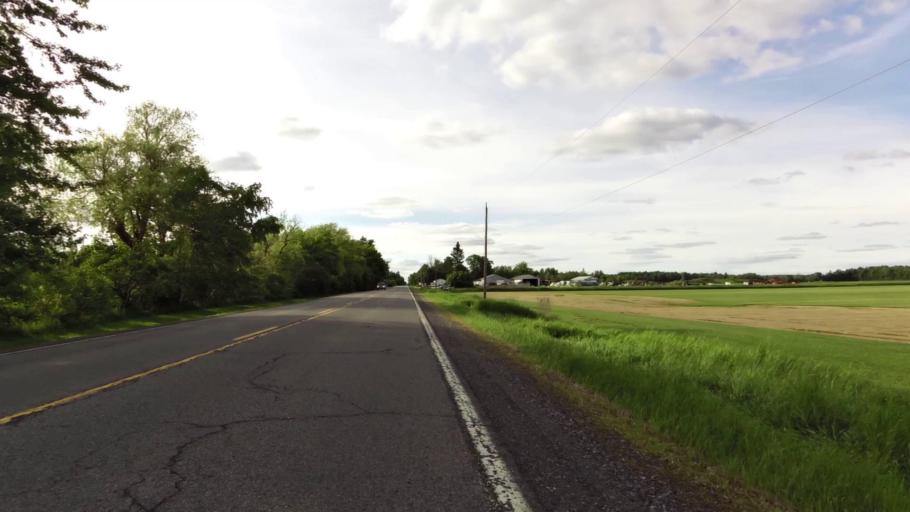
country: CA
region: Ontario
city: Ottawa
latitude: 45.1954
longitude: -75.5886
